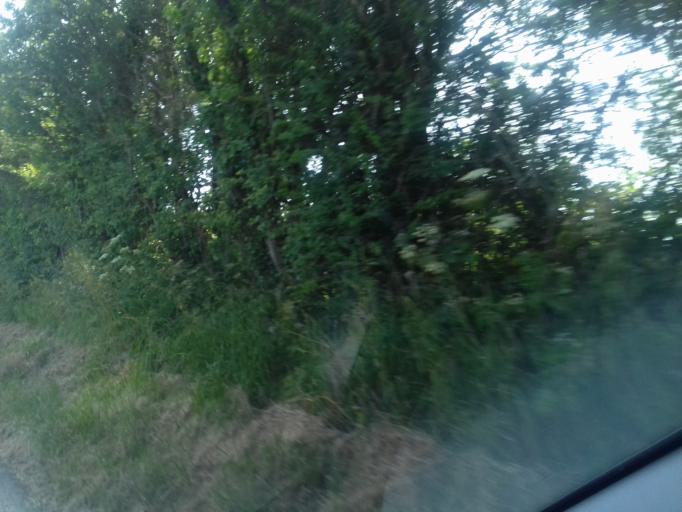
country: IE
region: Leinster
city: Lusk
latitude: 53.5221
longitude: -6.1800
